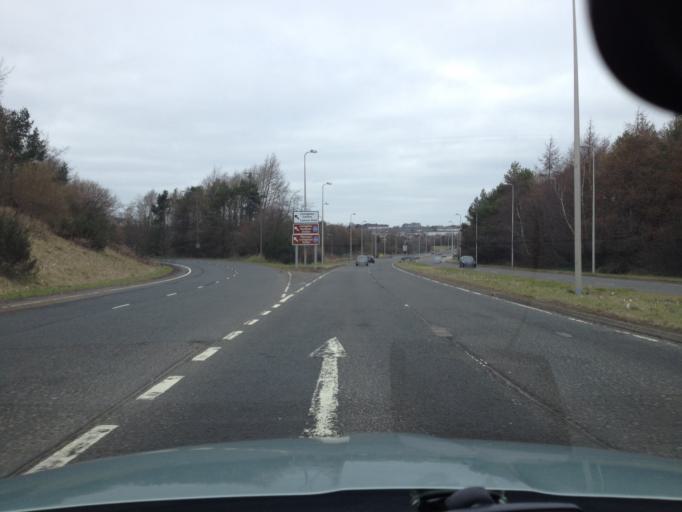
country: GB
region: Scotland
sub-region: West Lothian
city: Mid Calder
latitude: 55.8852
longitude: -3.4984
